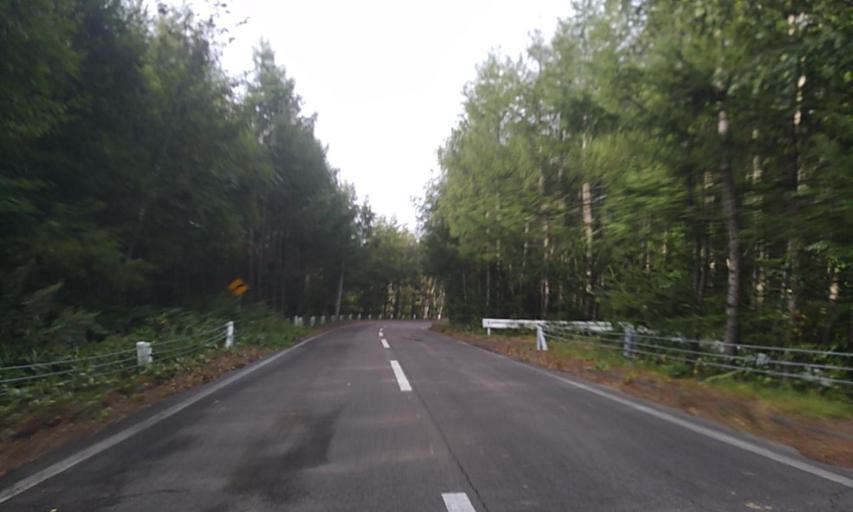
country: JP
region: Hokkaido
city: Abashiri
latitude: 43.7964
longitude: 144.5697
